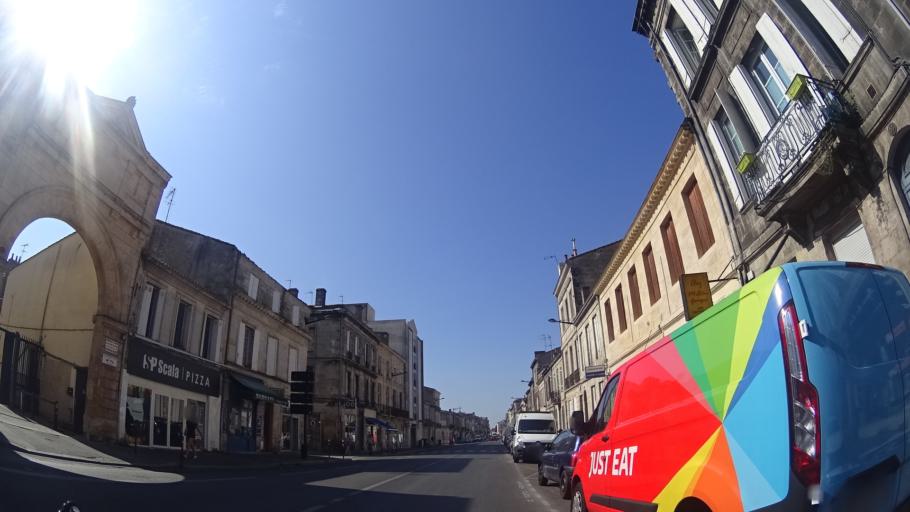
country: FR
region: Aquitaine
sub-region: Departement de la Gironde
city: Bordeaux
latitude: 44.8295
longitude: -0.5724
